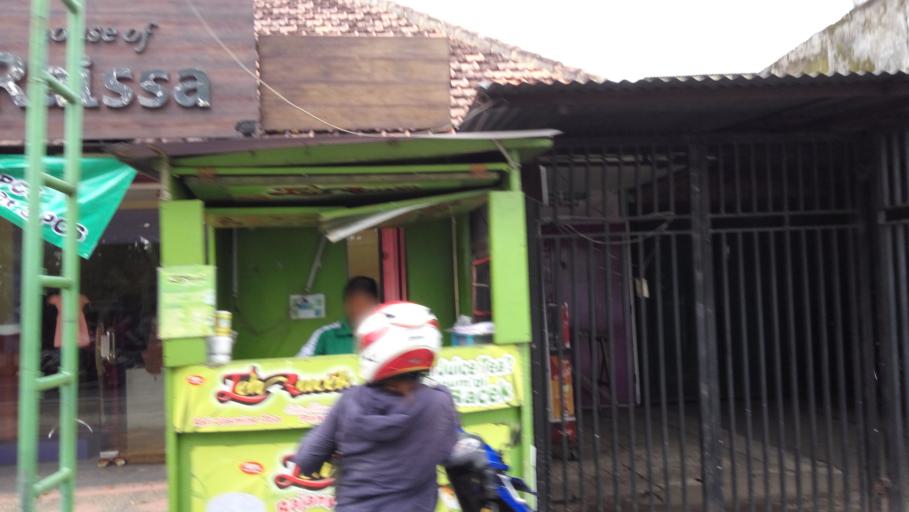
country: ID
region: East Java
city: Malang
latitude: -7.9231
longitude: 112.5969
